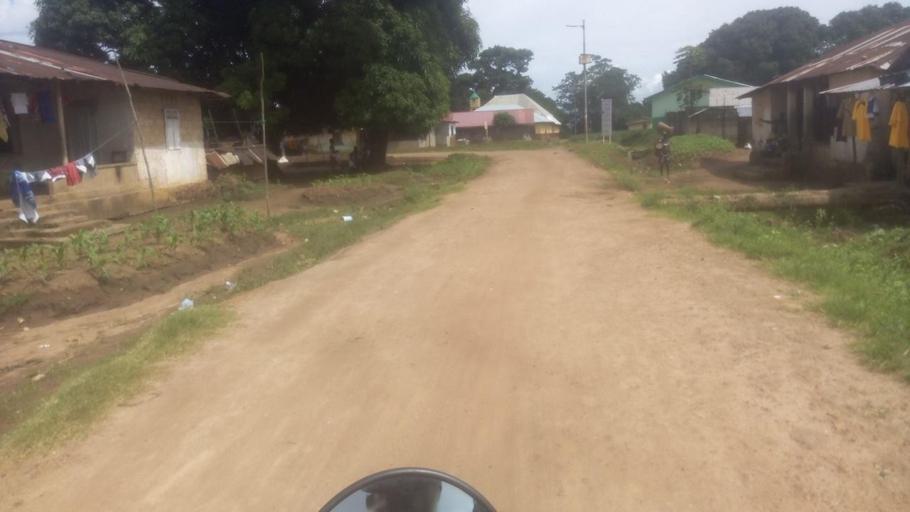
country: SL
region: Northern Province
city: Tintafor
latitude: 8.6401
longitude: -13.2269
